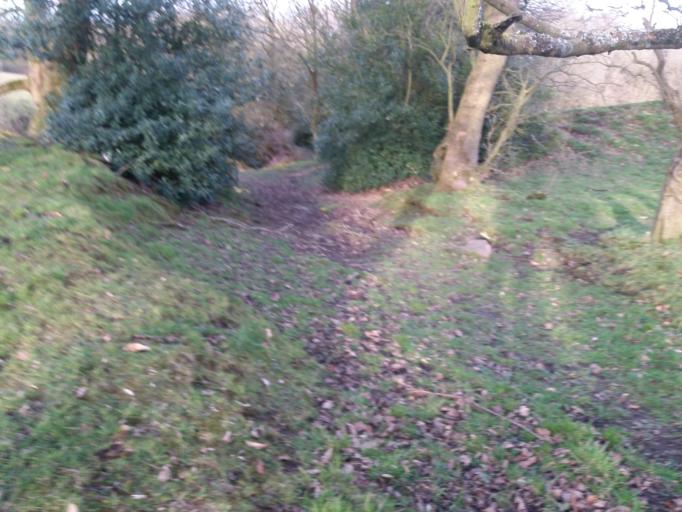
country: GB
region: England
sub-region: Lancashire
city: Coppull
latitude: 53.6471
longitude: -2.6670
